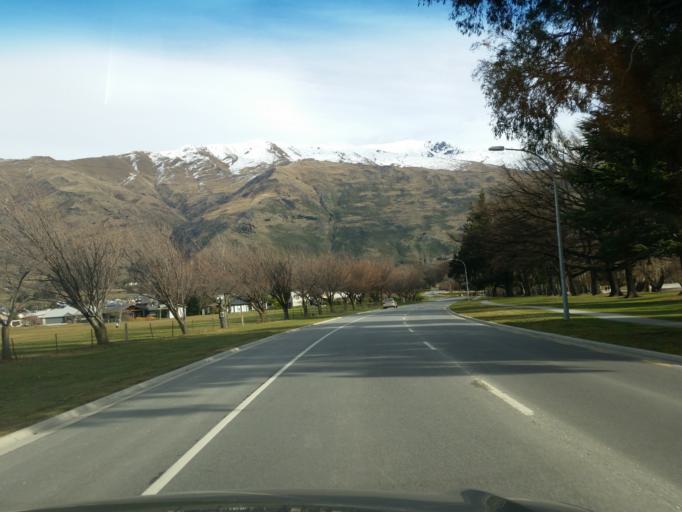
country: NZ
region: Otago
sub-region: Queenstown-Lakes District
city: Wanaka
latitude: -44.6993
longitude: 169.1260
